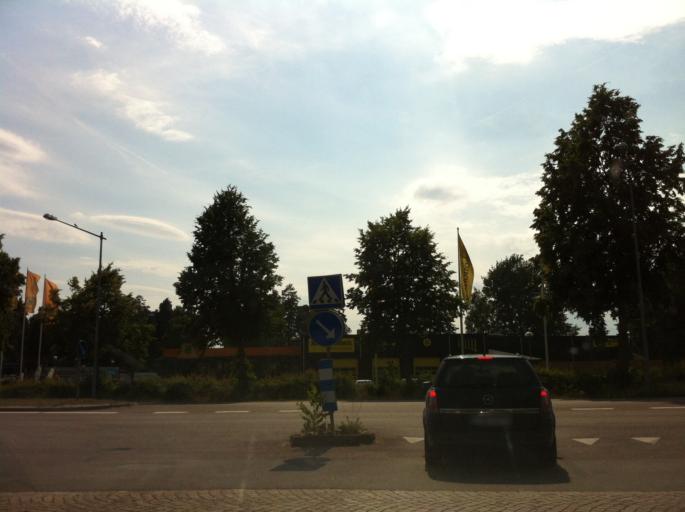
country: SE
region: Kalmar
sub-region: Nybro Kommun
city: Nybro
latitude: 56.7362
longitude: 15.9327
